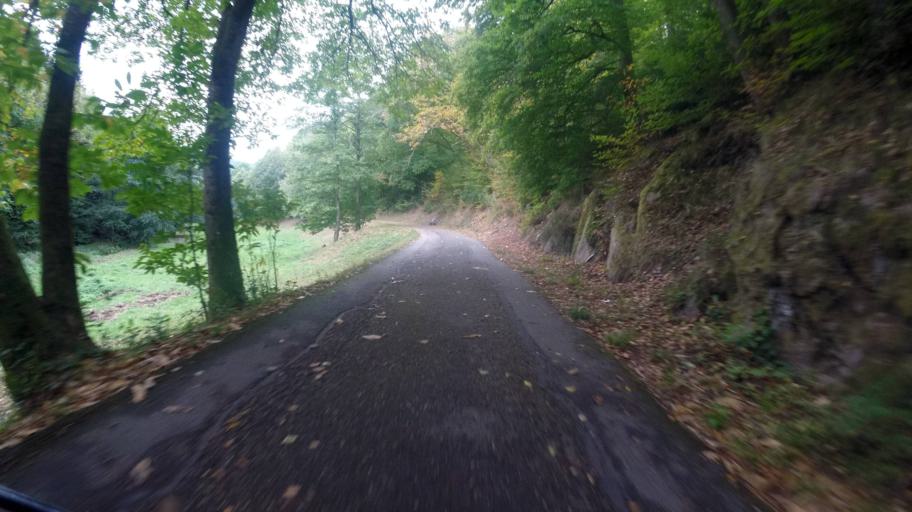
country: DE
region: Baden-Wuerttemberg
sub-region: Karlsruhe Region
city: Gernsbach
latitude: 48.7652
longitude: 8.3567
